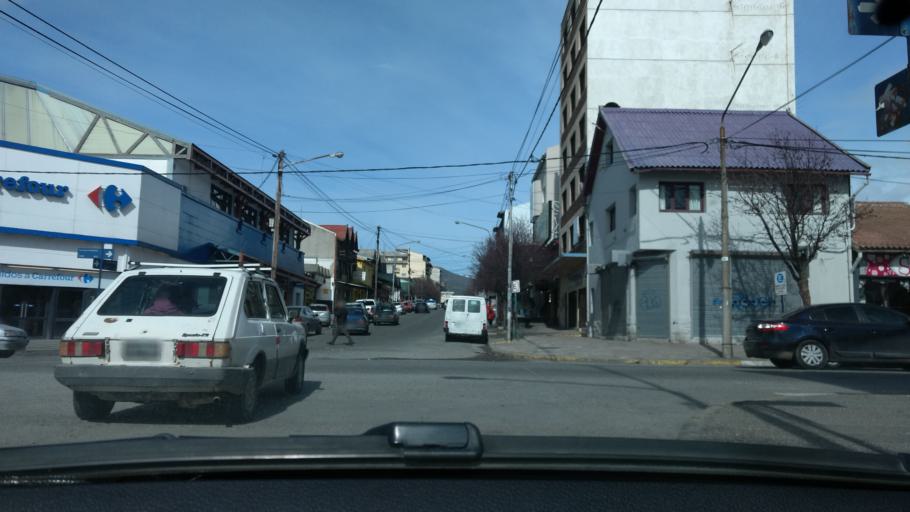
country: AR
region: Rio Negro
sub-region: Departamento de Bariloche
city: San Carlos de Bariloche
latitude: -41.1358
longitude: -71.2972
